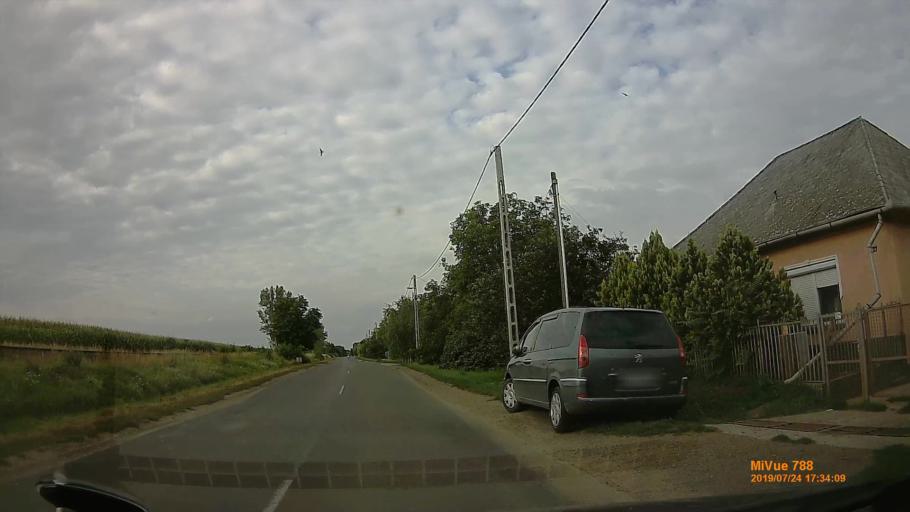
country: HU
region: Borsod-Abauj-Zemplen
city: Abaujszanto
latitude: 48.3013
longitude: 21.1963
